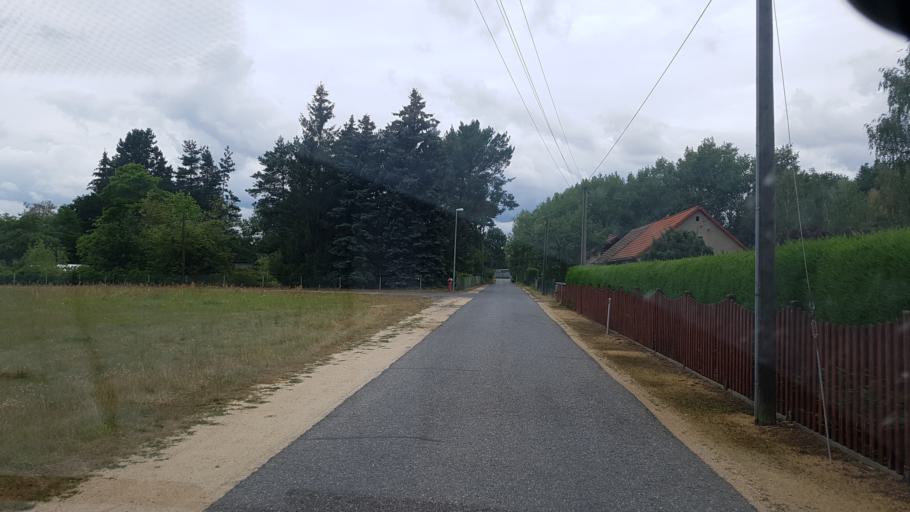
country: DE
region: Saxony
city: Rietschen
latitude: 51.3846
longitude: 14.7800
